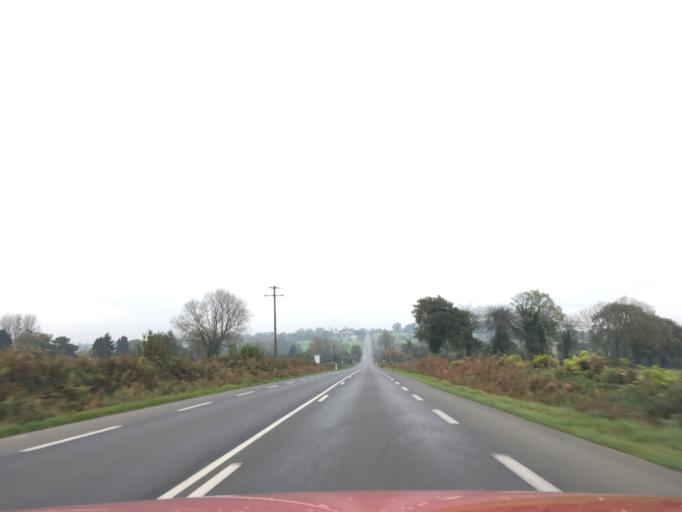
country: FR
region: Lower Normandy
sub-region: Departement de la Manche
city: Villedieu-les-Poeles
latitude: 48.8398
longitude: -1.2950
